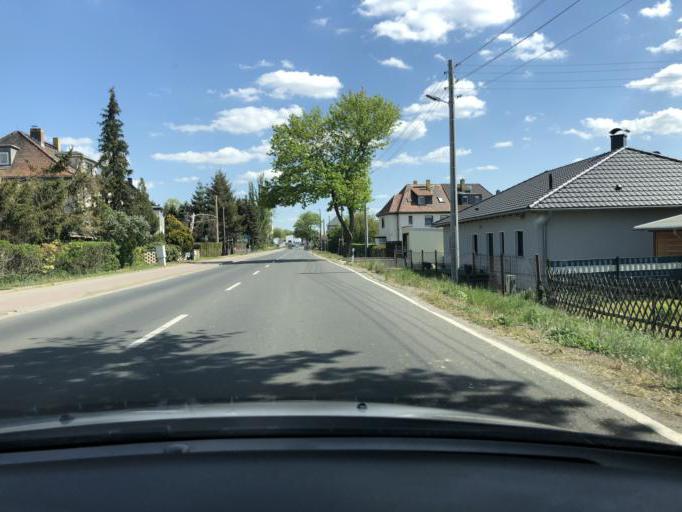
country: DE
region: Saxony
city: Schkeuditz
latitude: 51.3950
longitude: 12.2070
